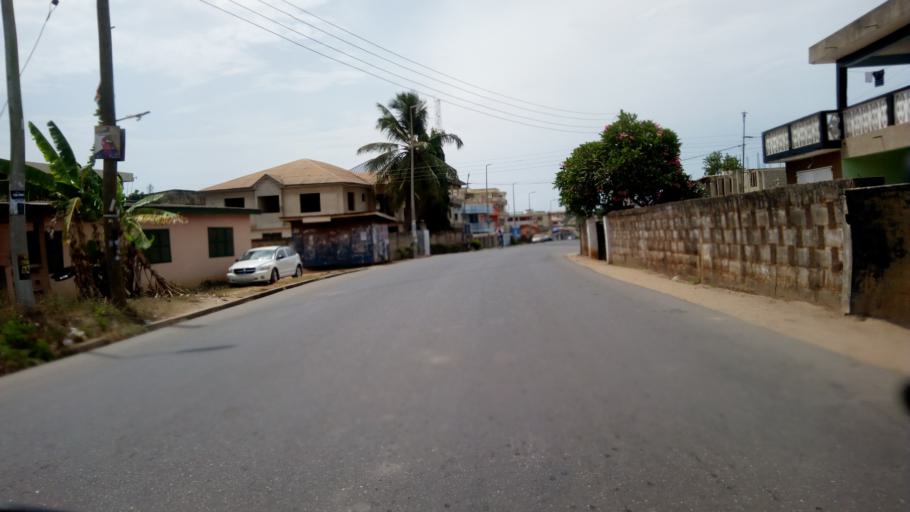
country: GH
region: Central
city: Cape Coast
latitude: 5.1318
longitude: -1.2766
